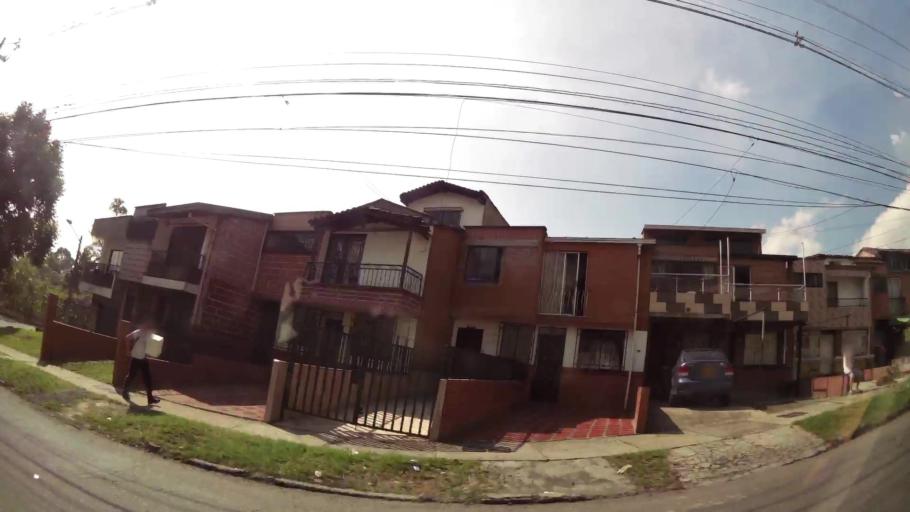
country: CO
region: Antioquia
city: La Estrella
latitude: 6.1688
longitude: -75.6401
